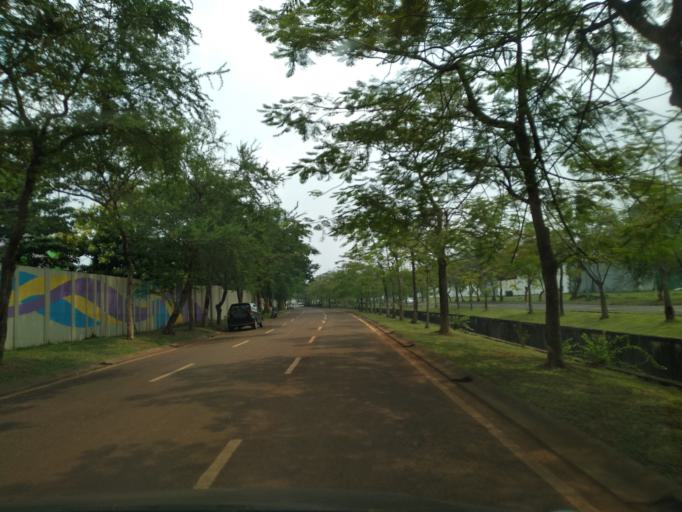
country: ID
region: West Java
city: Bekasi
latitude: -6.2978
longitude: 107.0517
